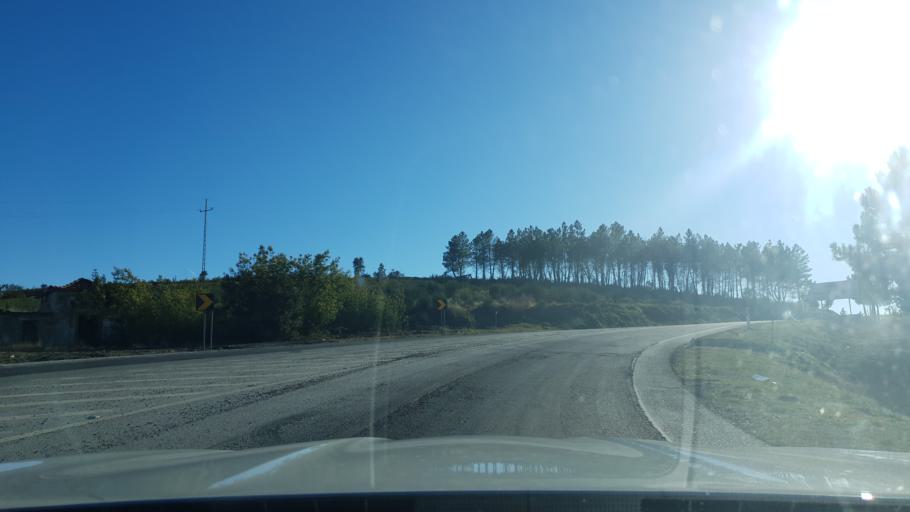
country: PT
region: Braganca
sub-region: Freixo de Espada A Cinta
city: Freixo de Espada a Cinta
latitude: 41.1541
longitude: -6.7976
